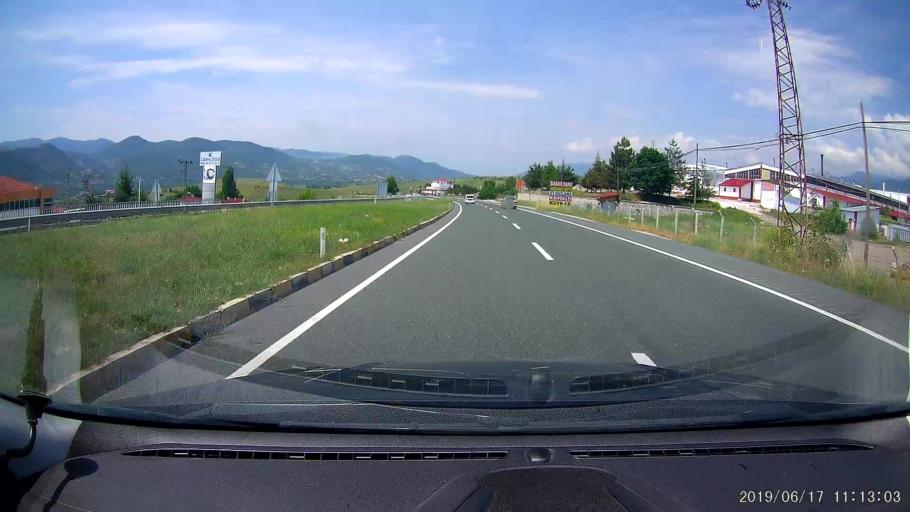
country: TR
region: Kastamonu
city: Tosya
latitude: 40.9674
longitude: 33.9807
